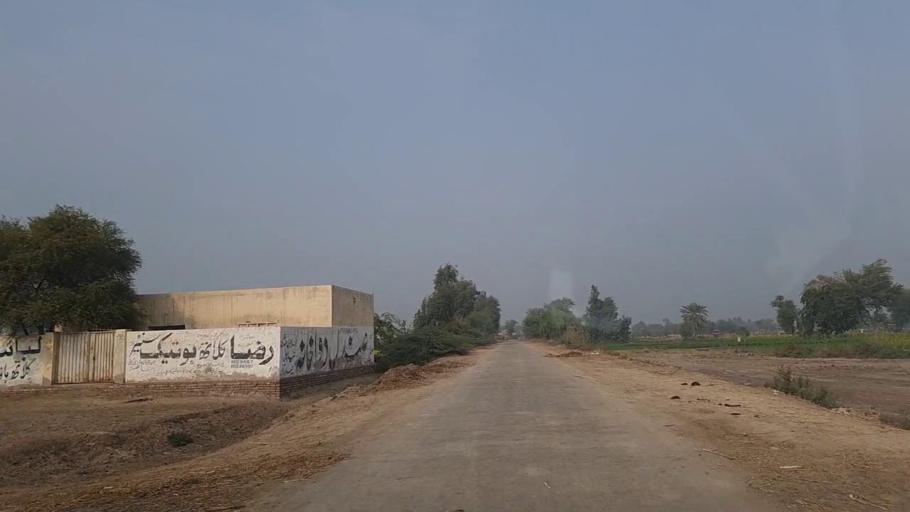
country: PK
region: Sindh
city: Sanghar
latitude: 26.0833
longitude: 68.8964
